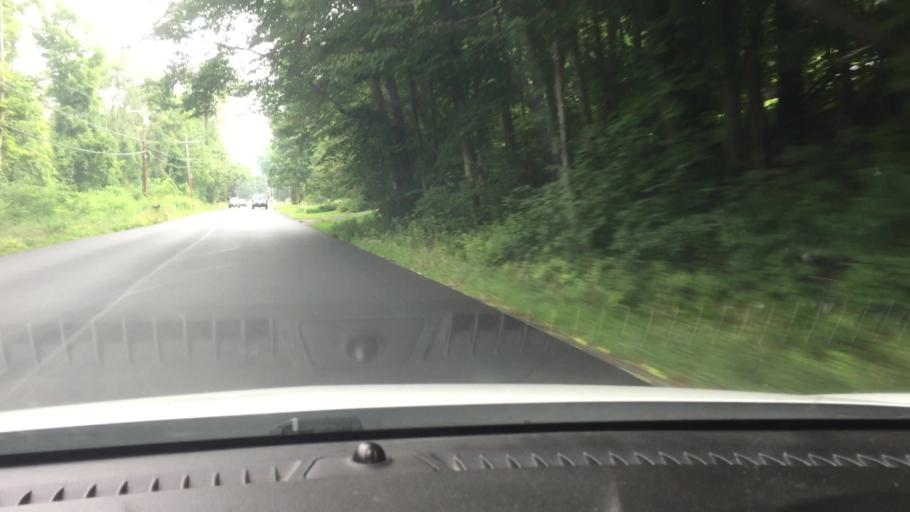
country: US
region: Massachusetts
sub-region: Berkshire County
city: Pittsfield
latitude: 42.4847
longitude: -73.2740
